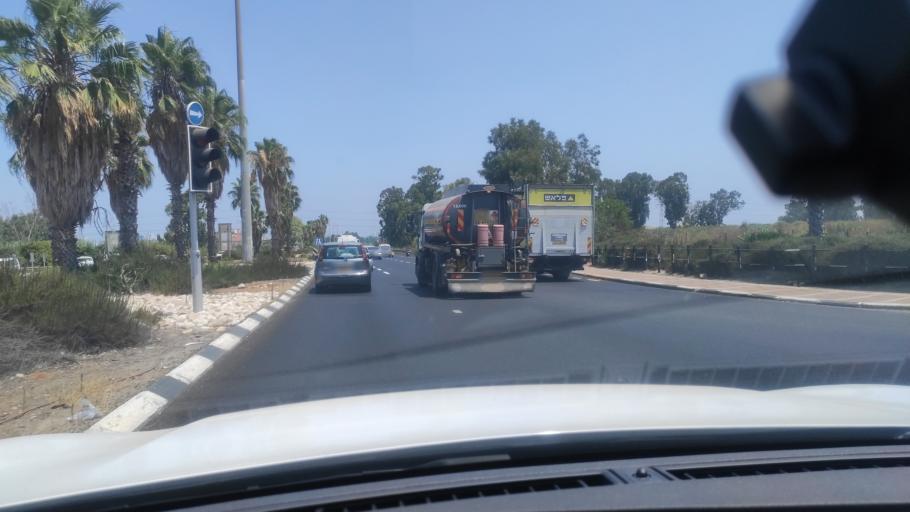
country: IL
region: Central District
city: Hod HaSharon
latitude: 32.1222
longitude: 34.9038
